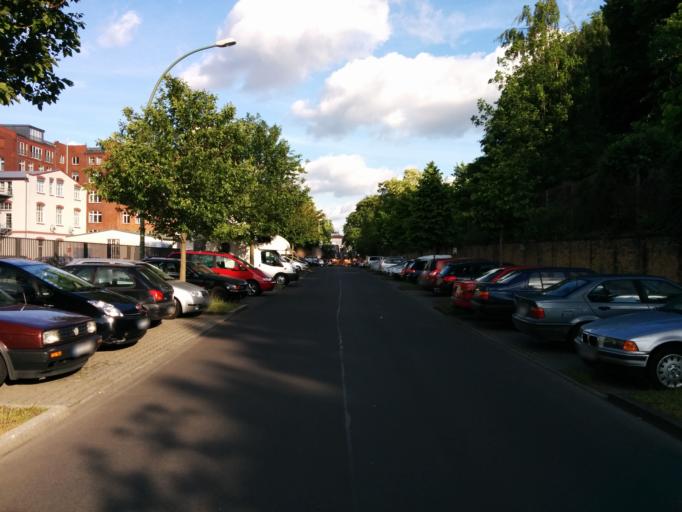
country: DE
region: Berlin
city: Berlin Treptow
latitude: 52.4927
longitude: 13.4493
